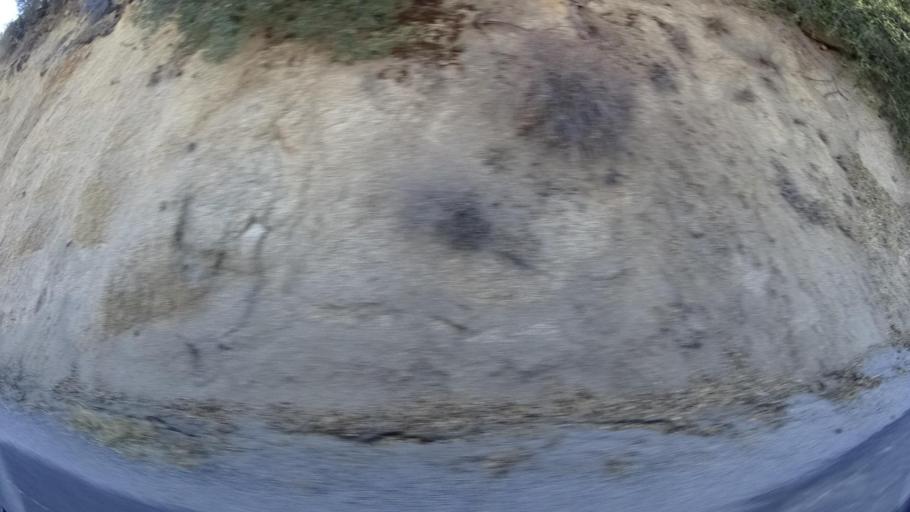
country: US
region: California
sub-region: Kern County
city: Bodfish
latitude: 35.5941
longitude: -118.5066
